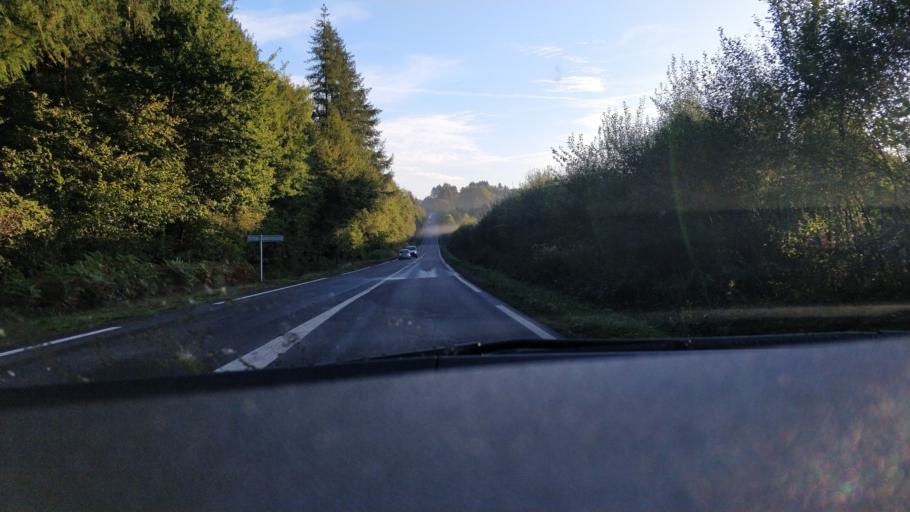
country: FR
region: Limousin
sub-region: Departement de la Haute-Vienne
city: Sauviat-sur-Vige
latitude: 45.8867
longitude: 1.5650
